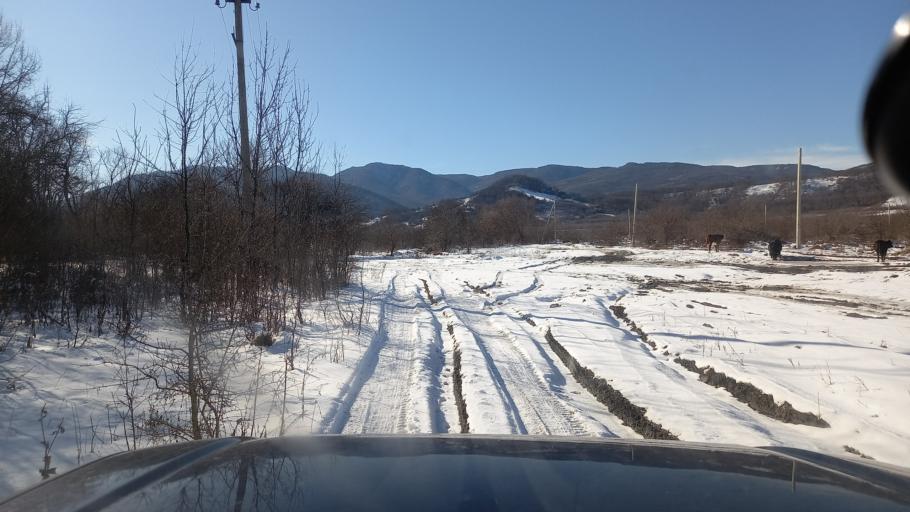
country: RU
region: Adygeya
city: Kamennomostskiy
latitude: 44.2163
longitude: 40.1740
